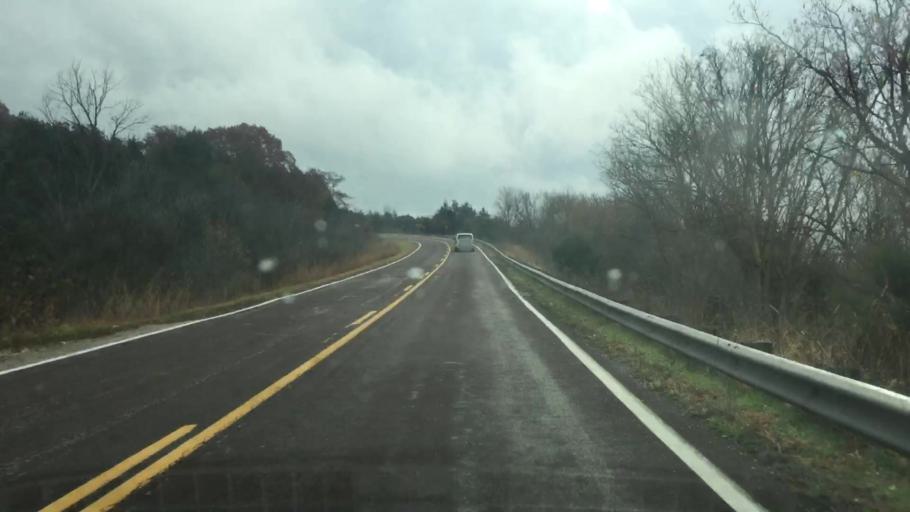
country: US
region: Missouri
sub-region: Callaway County
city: Fulton
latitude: 38.7793
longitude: -91.8495
